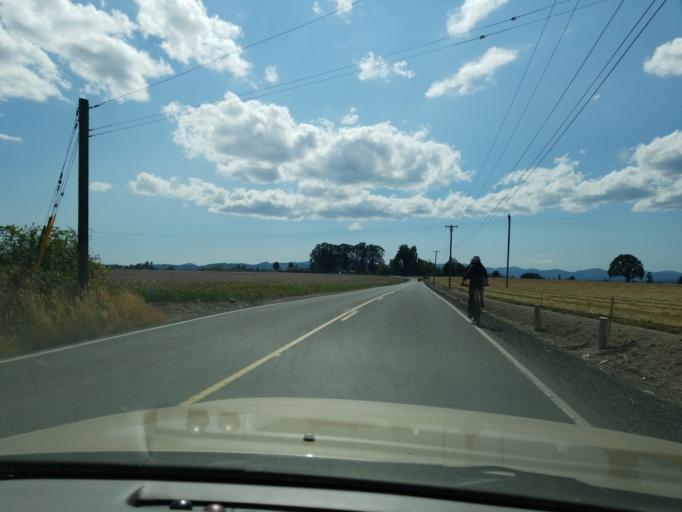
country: US
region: Oregon
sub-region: Yamhill County
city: Carlton
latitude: 45.2950
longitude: -123.1531
